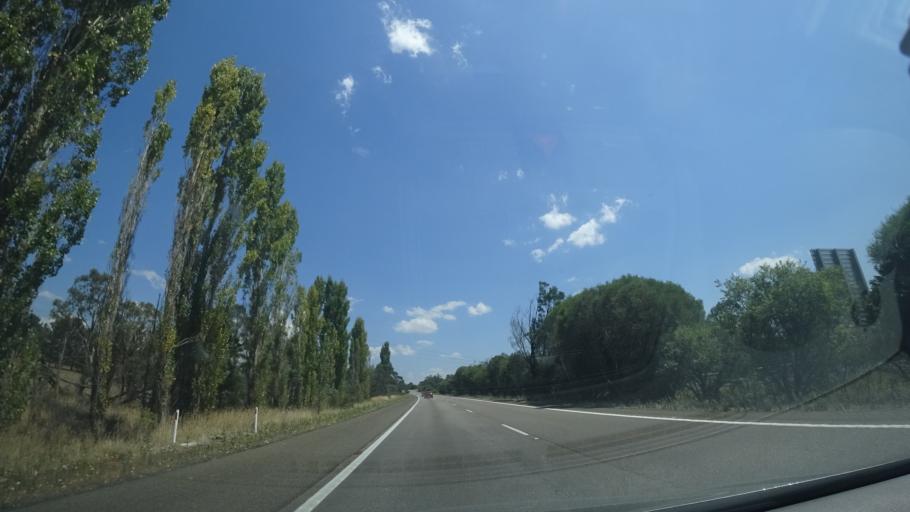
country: AU
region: New South Wales
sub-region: Wingecarribee
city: Bundanoon
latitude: -34.5942
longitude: 150.2430
